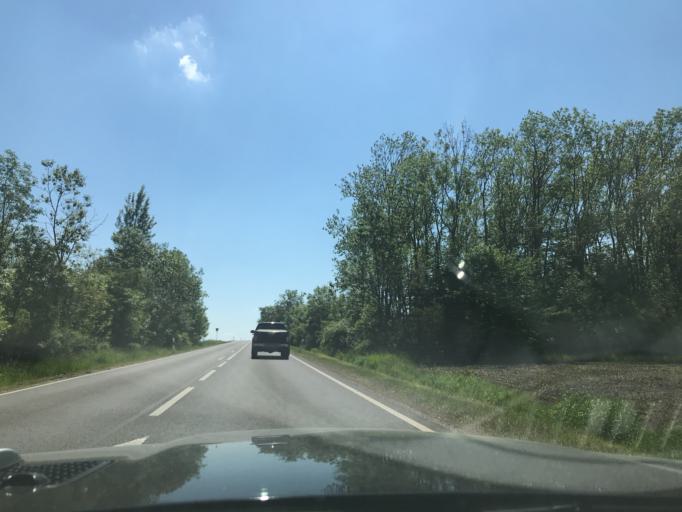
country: DE
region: Thuringia
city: Hochheim
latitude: 51.0471
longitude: 10.6584
